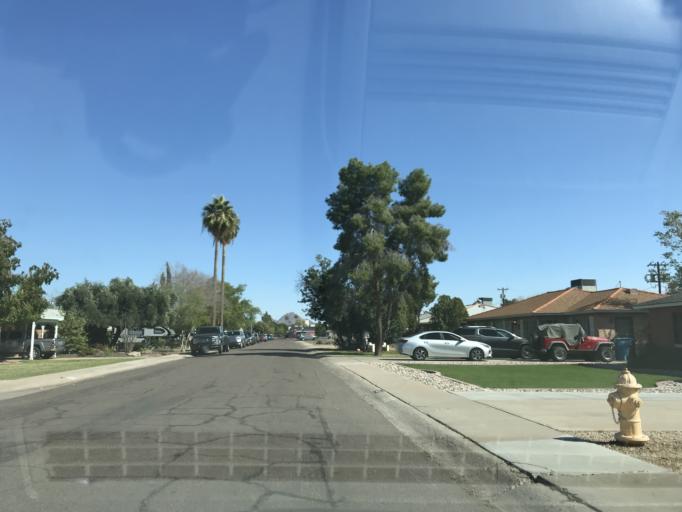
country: US
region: Arizona
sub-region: Maricopa County
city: Phoenix
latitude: 33.5175
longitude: -112.0849
